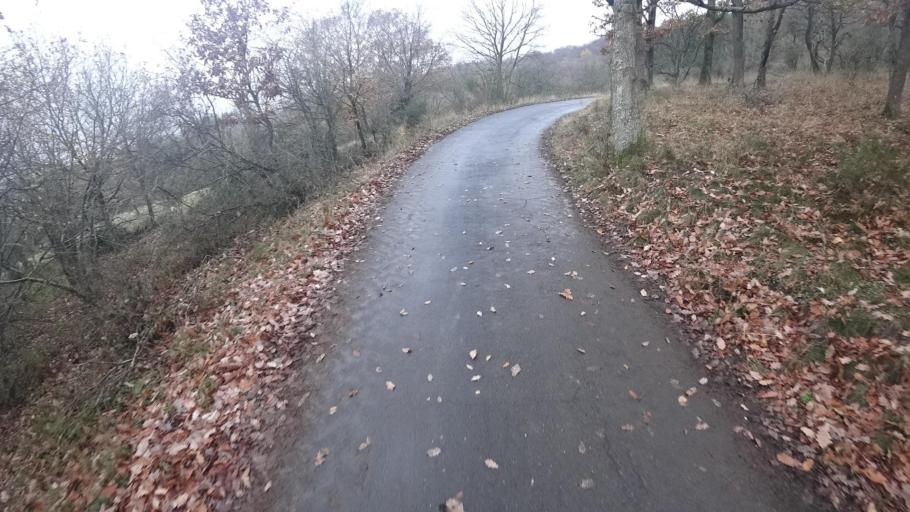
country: DE
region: Rheinland-Pfalz
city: Kesseling
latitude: 50.4927
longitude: 7.0163
